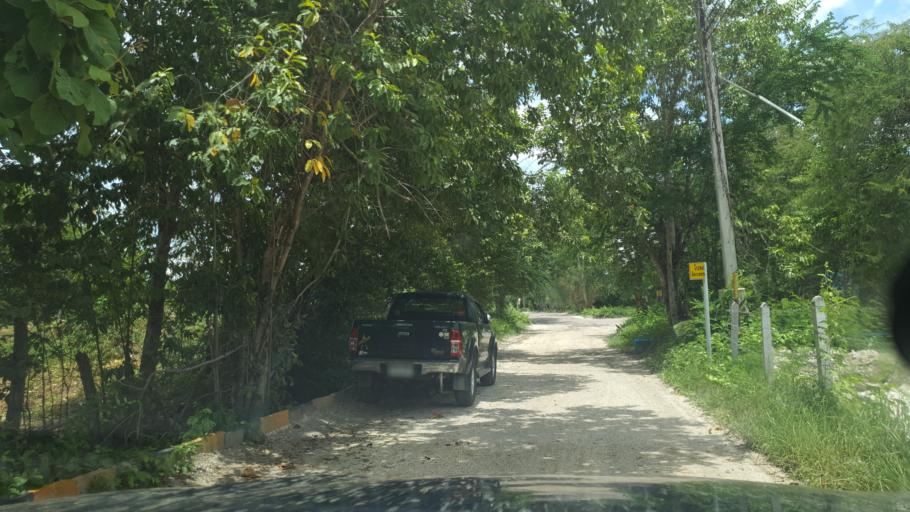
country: TH
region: Lampang
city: Sop Prap
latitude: 17.9409
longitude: 99.3535
